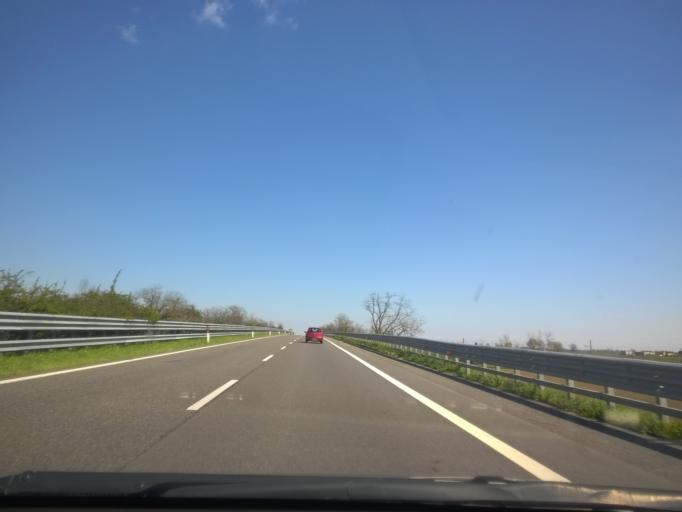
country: IT
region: Emilia-Romagna
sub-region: Provincia di Piacenza
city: Caorso
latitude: 45.0578
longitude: 9.9068
